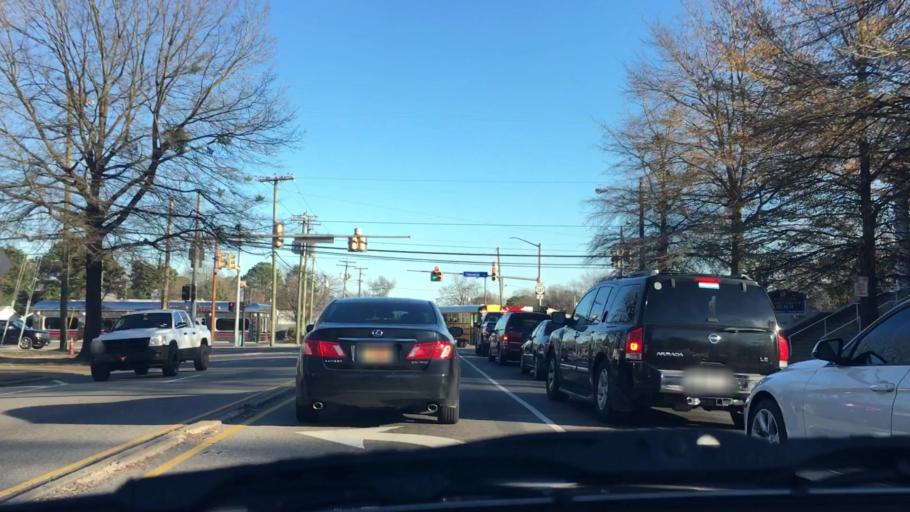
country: US
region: Virginia
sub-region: City of Norfolk
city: Norfolk
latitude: 36.8779
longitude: -76.2642
